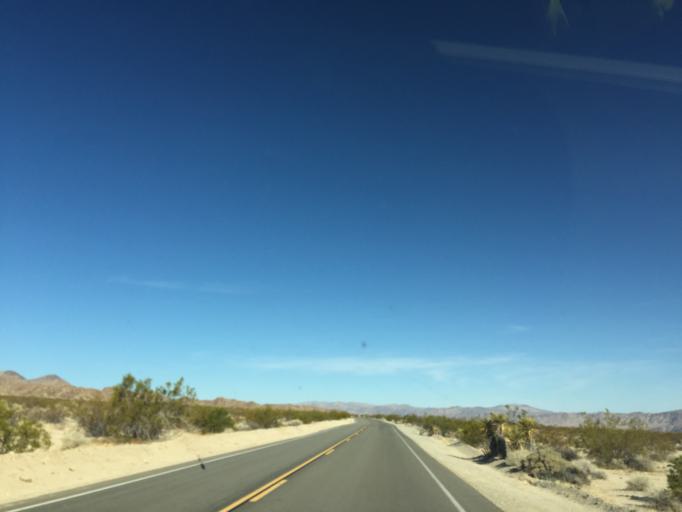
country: US
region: California
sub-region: San Bernardino County
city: Twentynine Palms
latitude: 33.8519
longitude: -115.7850
